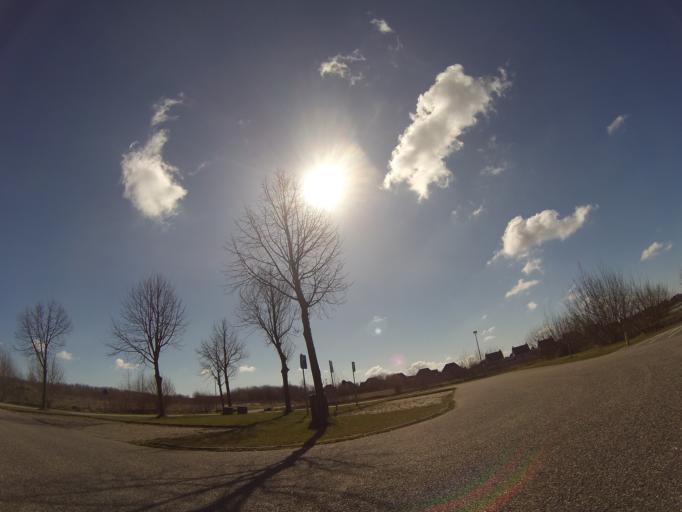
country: NL
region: Drenthe
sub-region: Gemeente Emmen
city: Emmen
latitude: 52.7388
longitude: 6.9069
